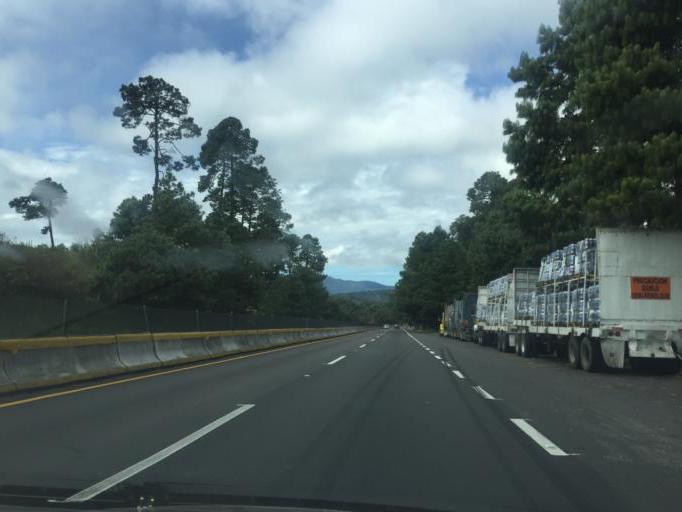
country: MX
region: Morelos
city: Tres Marias
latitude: 19.0842
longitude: -99.2262
